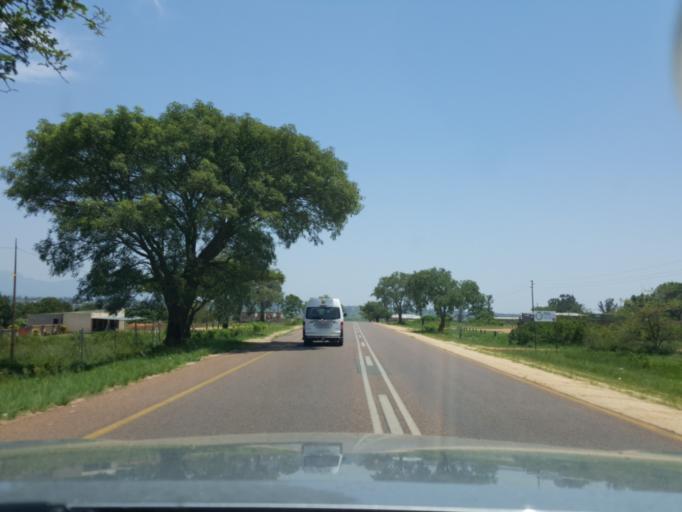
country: ZA
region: Limpopo
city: Thulamahashi
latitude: -24.7610
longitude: 31.0432
